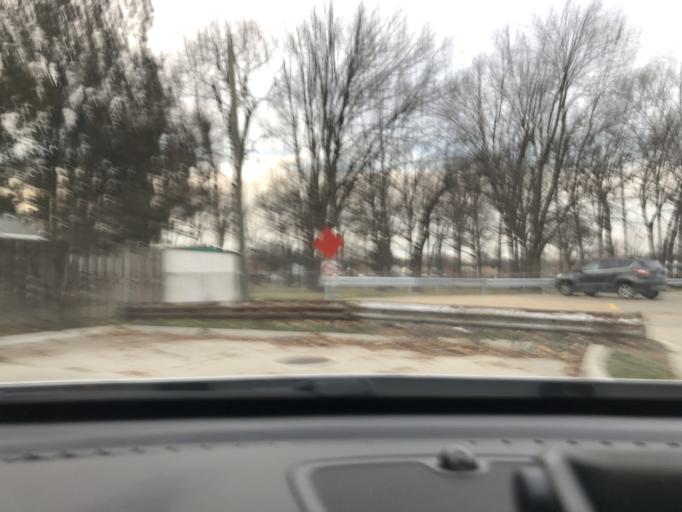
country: US
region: Michigan
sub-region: Wayne County
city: Allen Park
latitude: 42.2864
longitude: -83.2244
